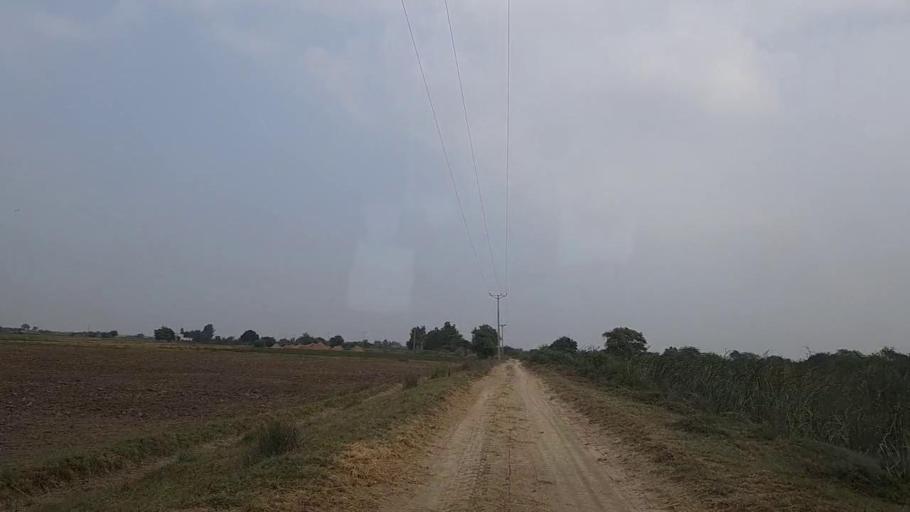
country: PK
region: Sindh
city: Mirpur Sakro
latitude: 24.6105
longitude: 67.7129
